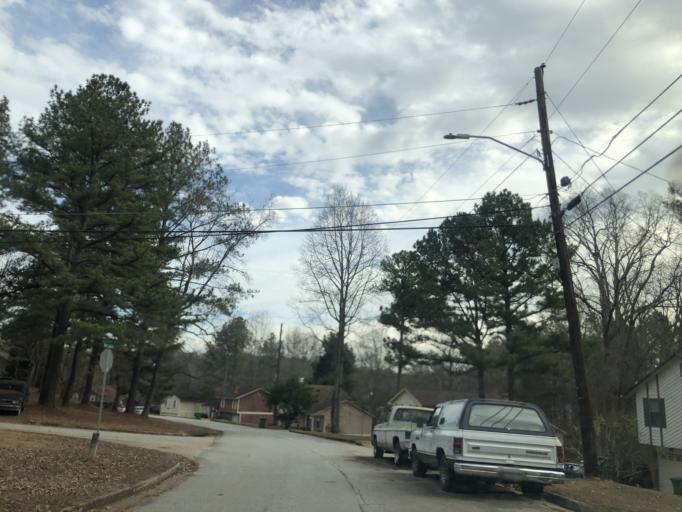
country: US
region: Georgia
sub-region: DeKalb County
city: Panthersville
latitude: 33.6709
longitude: -84.2119
